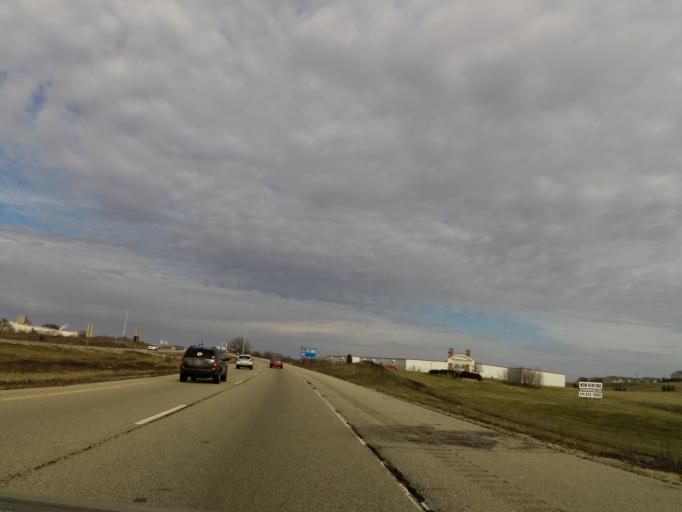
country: US
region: Wisconsin
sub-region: Rock County
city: Beloit
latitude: 42.5161
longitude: -88.9760
